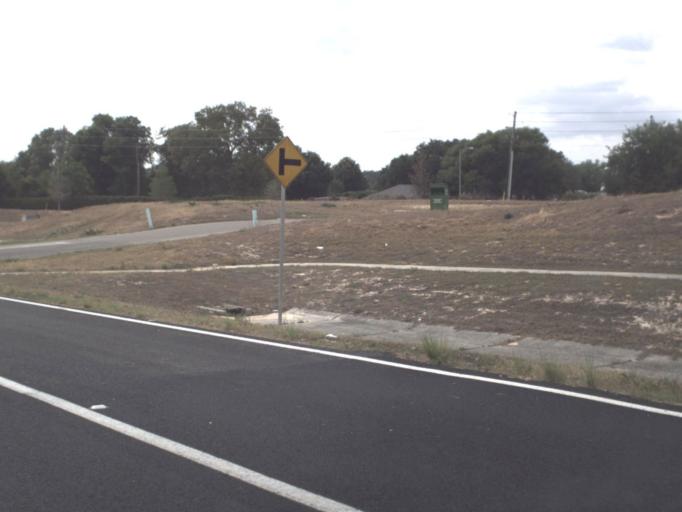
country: US
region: Florida
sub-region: Lake County
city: Groveland
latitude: 28.5581
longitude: -81.8246
